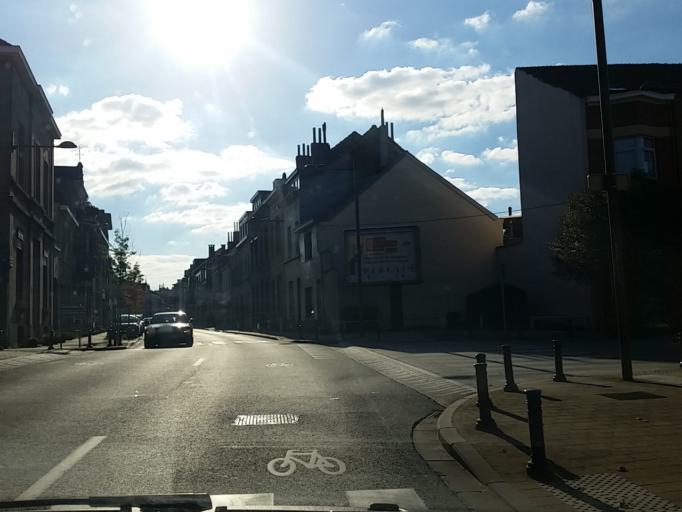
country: BE
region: Flanders
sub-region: Provincie Vlaams-Brabant
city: Diegem
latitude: 50.8741
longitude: 4.4014
